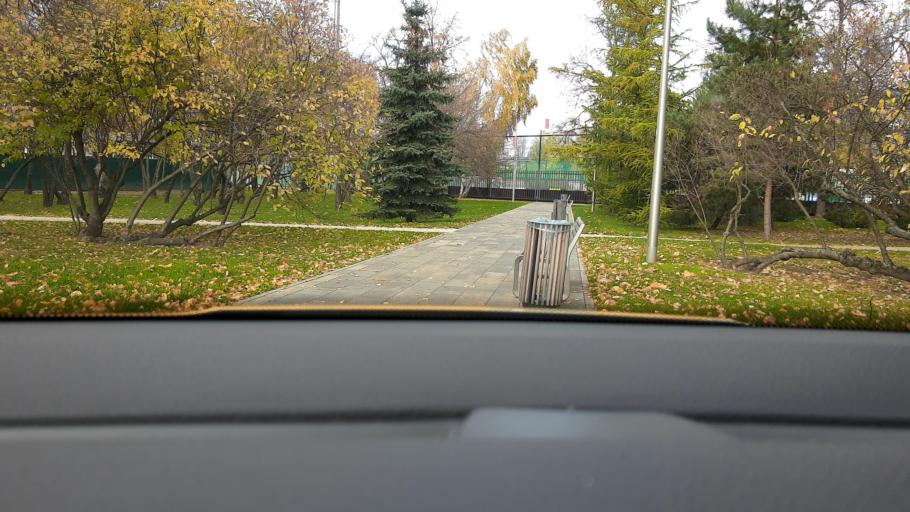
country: RU
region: Moscow
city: Luzhniki
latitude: 55.7187
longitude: 37.5536
